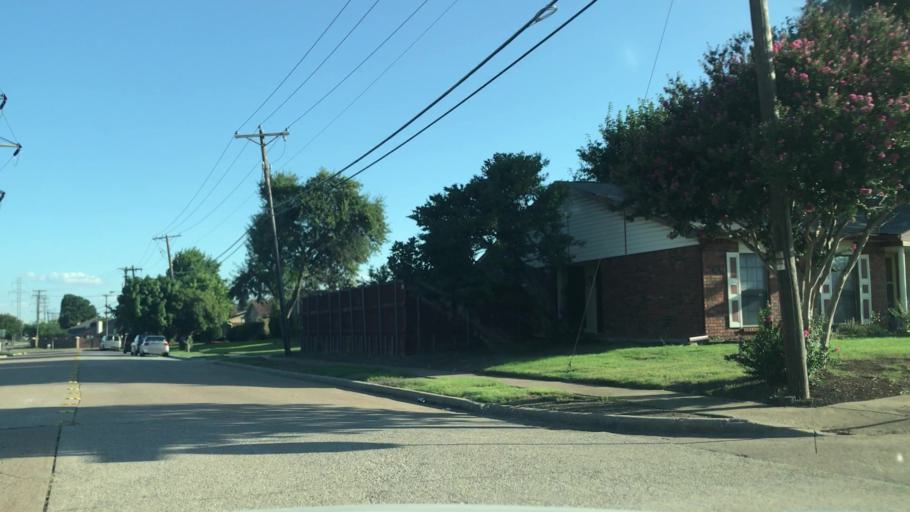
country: US
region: Texas
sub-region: Collin County
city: Plano
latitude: 33.0426
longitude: -96.7101
